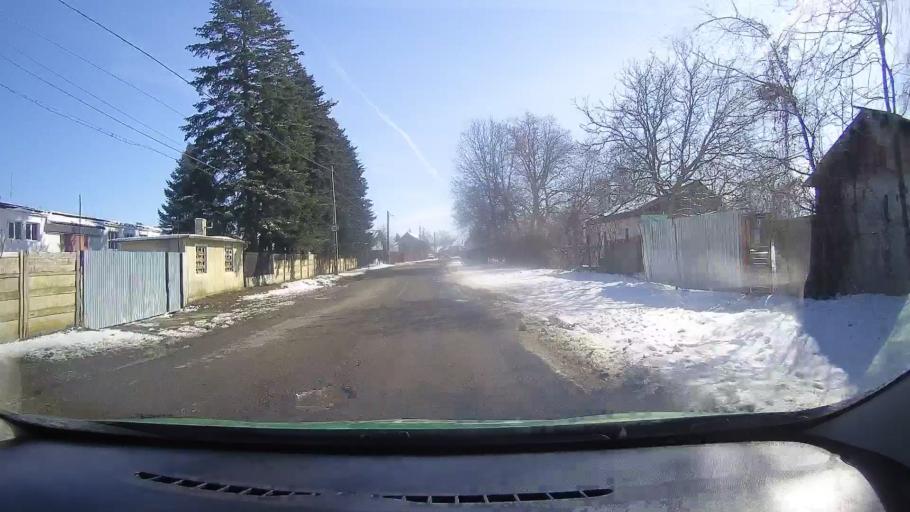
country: RO
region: Brasov
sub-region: Comuna Recea
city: Recea
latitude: 45.7341
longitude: 24.9339
